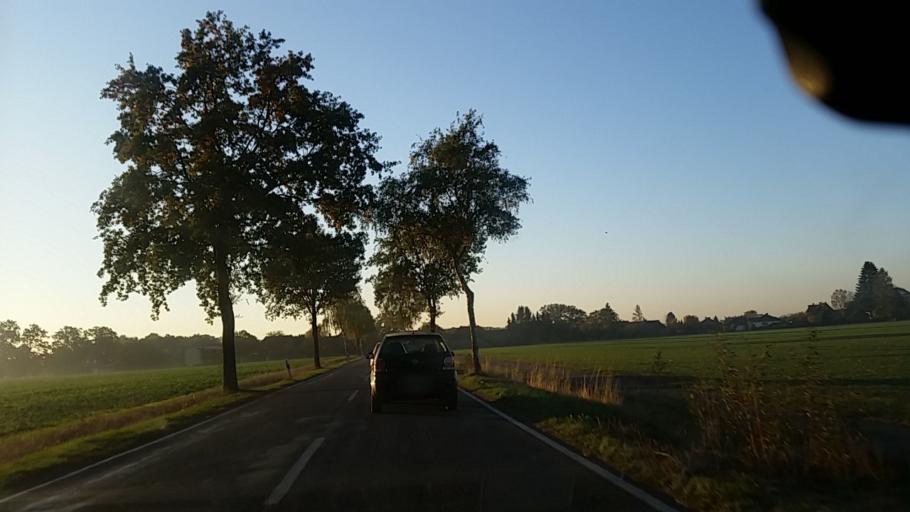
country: DE
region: Lower Saxony
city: Wittingen
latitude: 52.6703
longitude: 10.7996
